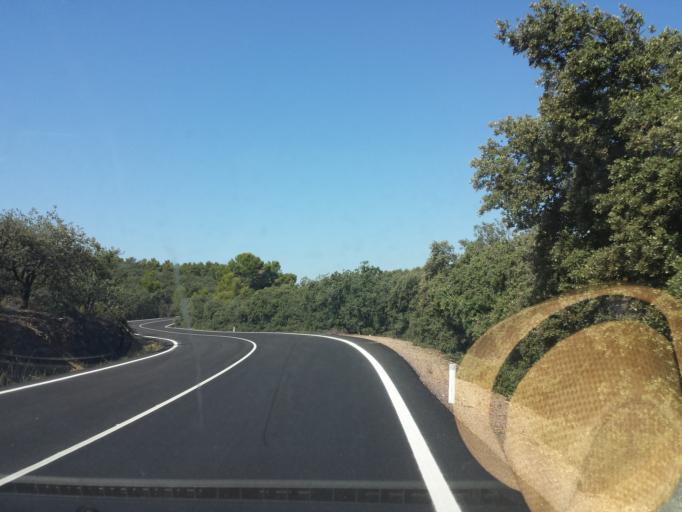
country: ES
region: Aragon
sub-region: Provincia de Zaragoza
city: Munebrega
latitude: 41.2255
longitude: -1.7320
